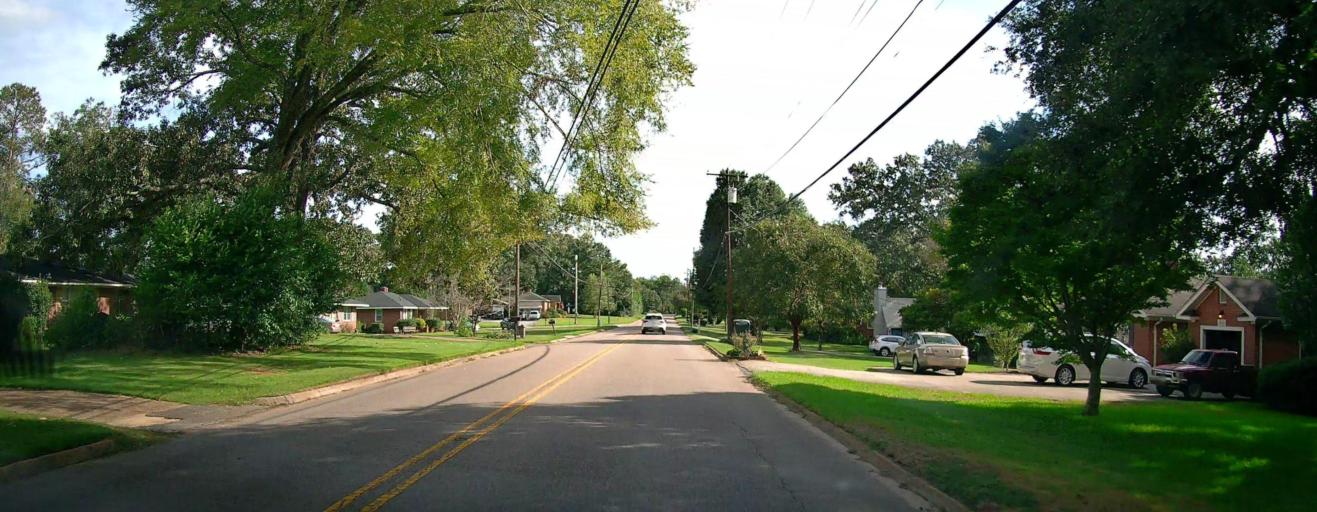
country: US
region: Alabama
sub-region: Russell County
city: Phenix City
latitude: 32.5079
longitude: -85.0195
